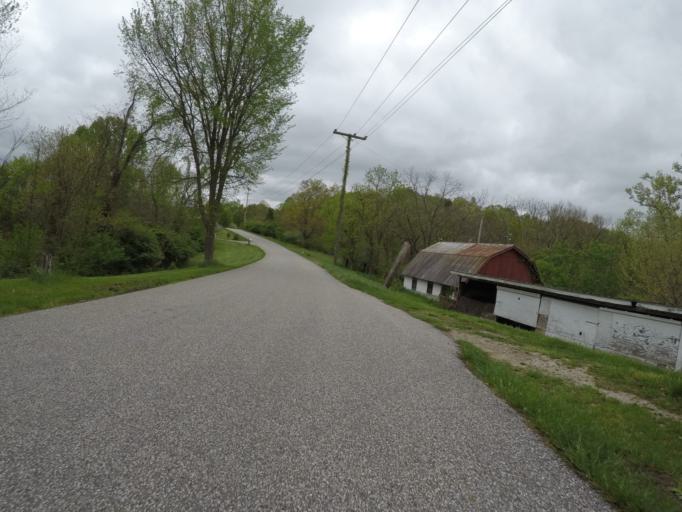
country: US
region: West Virginia
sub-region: Cabell County
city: Barboursville
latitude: 38.4021
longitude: -82.2661
